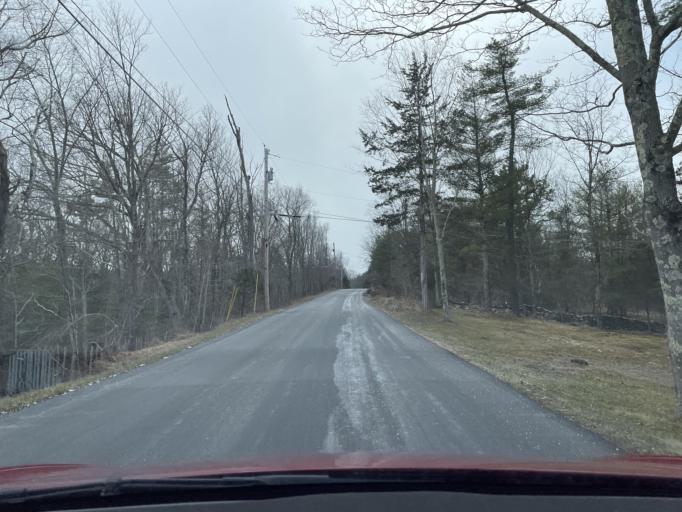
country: US
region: New York
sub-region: Ulster County
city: Manorville
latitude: 42.0948
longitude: -74.0257
